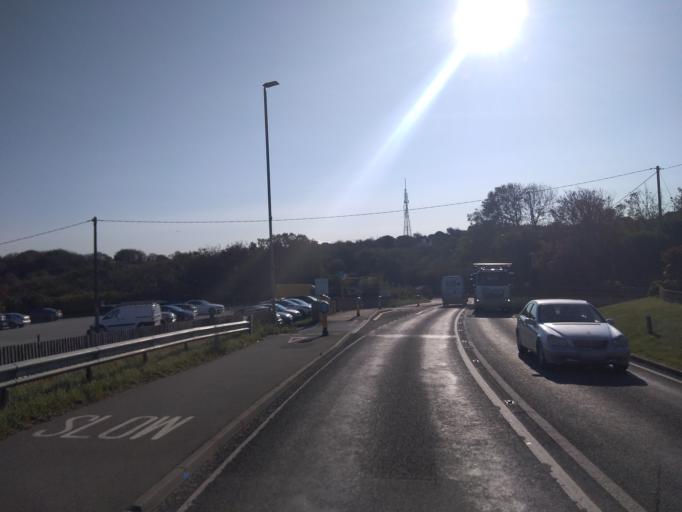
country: GB
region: England
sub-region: East Sussex
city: Newhaven
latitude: 50.7903
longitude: 0.0308
